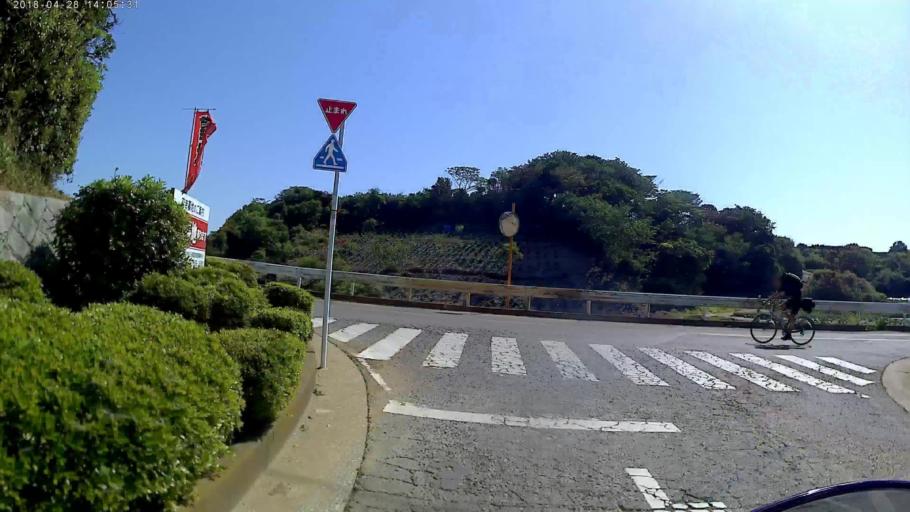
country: JP
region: Kanagawa
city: Miura
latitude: 35.1578
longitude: 139.6509
